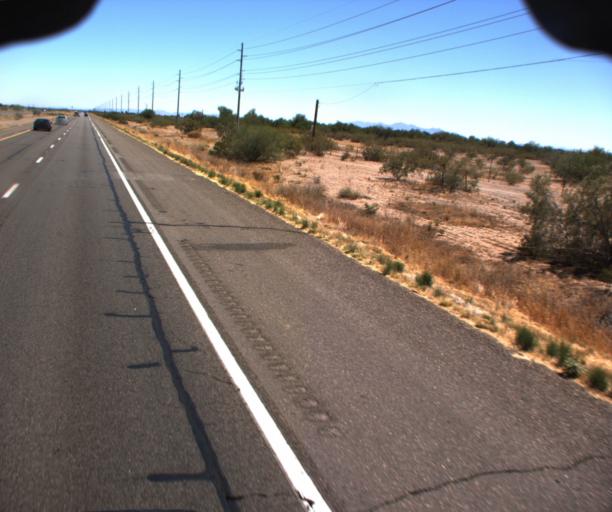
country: US
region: Arizona
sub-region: Maricopa County
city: Sun City West
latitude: 33.7248
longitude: -112.4608
